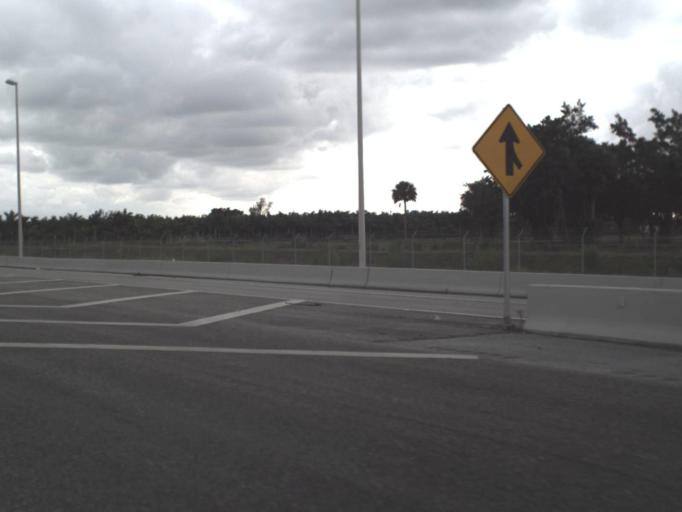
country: US
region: Florida
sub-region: Palm Beach County
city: Greenacres City
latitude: 26.6110
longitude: -80.1737
